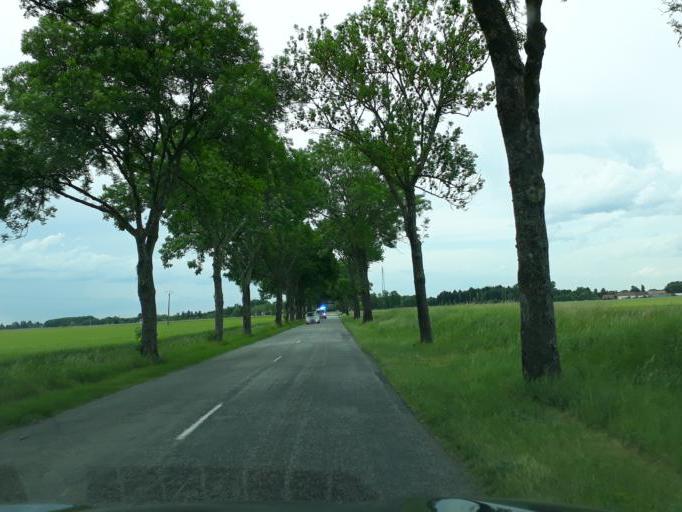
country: FR
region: Centre
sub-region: Departement du Loiret
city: Vienne-en-Val
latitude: 47.8301
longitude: 2.1460
